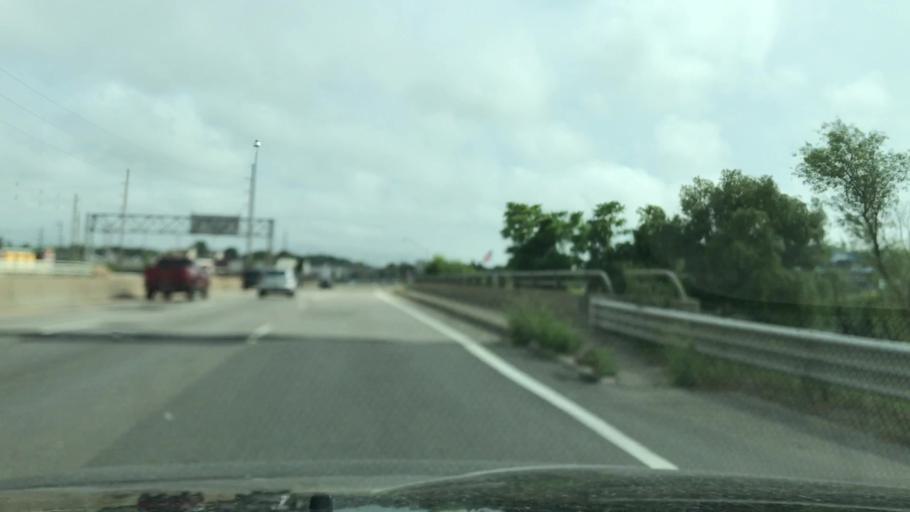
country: US
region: Michigan
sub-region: Ottawa County
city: Grand Haven
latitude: 43.0703
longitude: -86.2196
